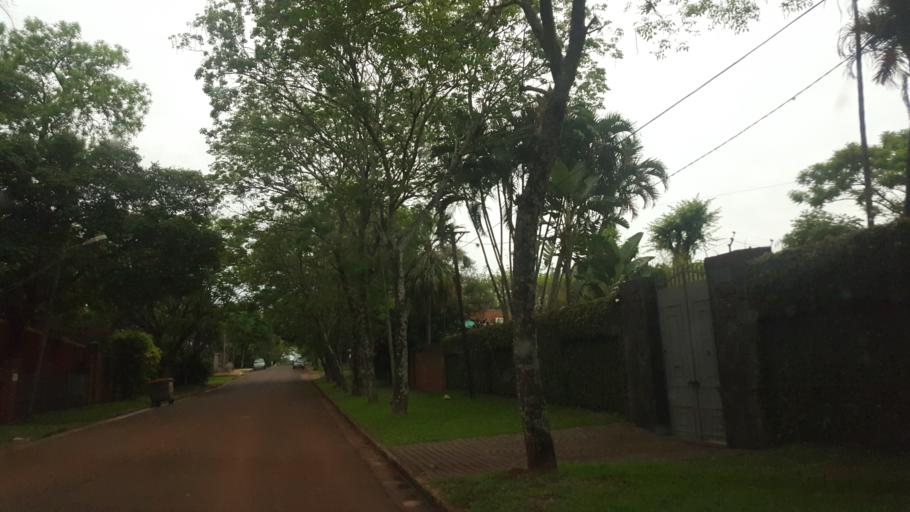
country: AR
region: Misiones
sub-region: Departamento de Capital
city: Posadas
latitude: -27.3548
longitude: -55.9223
